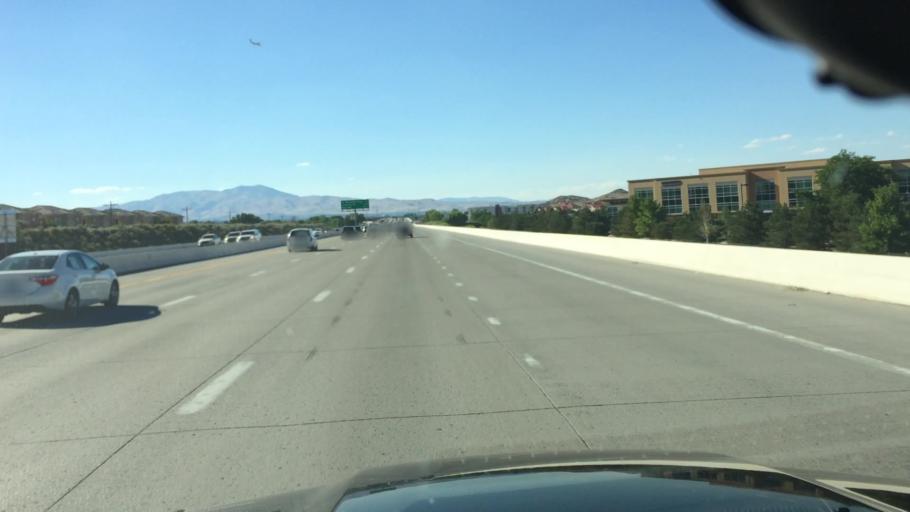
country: US
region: Nevada
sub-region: Washoe County
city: Sparks
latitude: 39.4290
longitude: -119.7576
